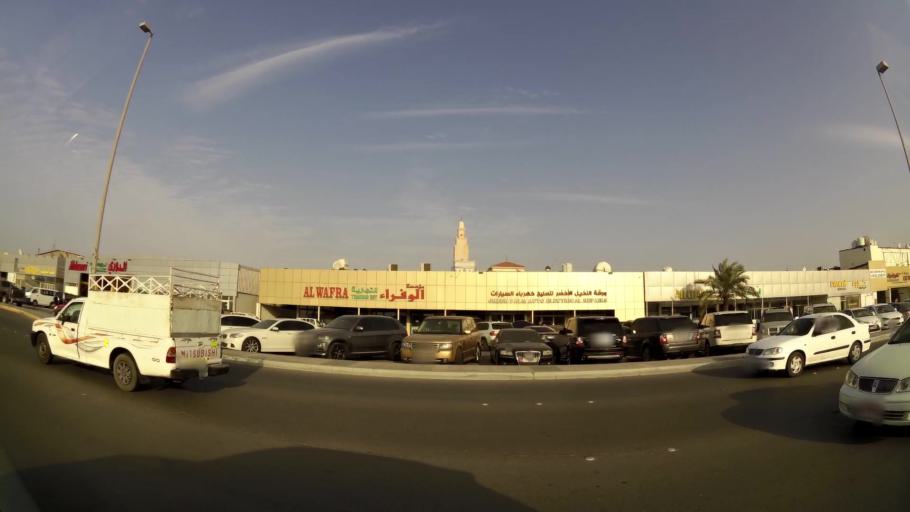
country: AE
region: Abu Dhabi
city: Abu Dhabi
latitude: 24.3750
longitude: 54.5111
